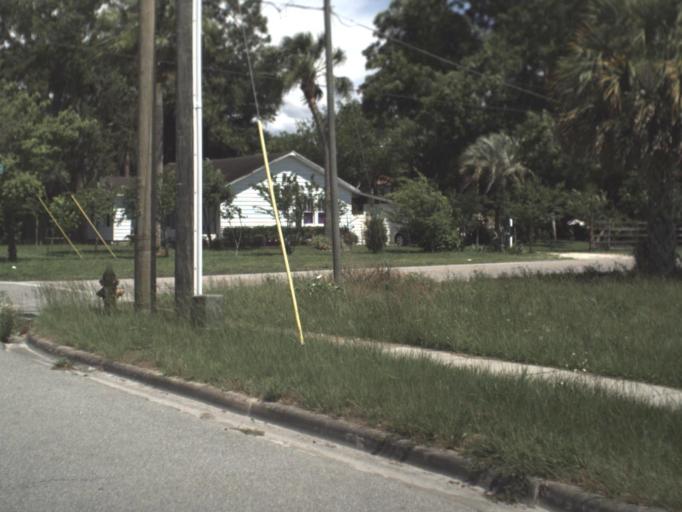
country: US
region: Florida
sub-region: Lafayette County
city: Mayo
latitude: 30.0531
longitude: -83.1697
